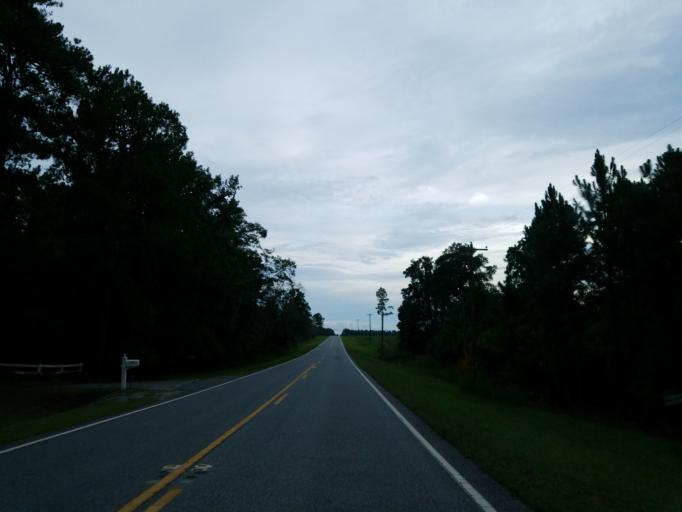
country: US
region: Georgia
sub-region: Lanier County
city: Lakeland
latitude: 30.8977
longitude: -83.0058
